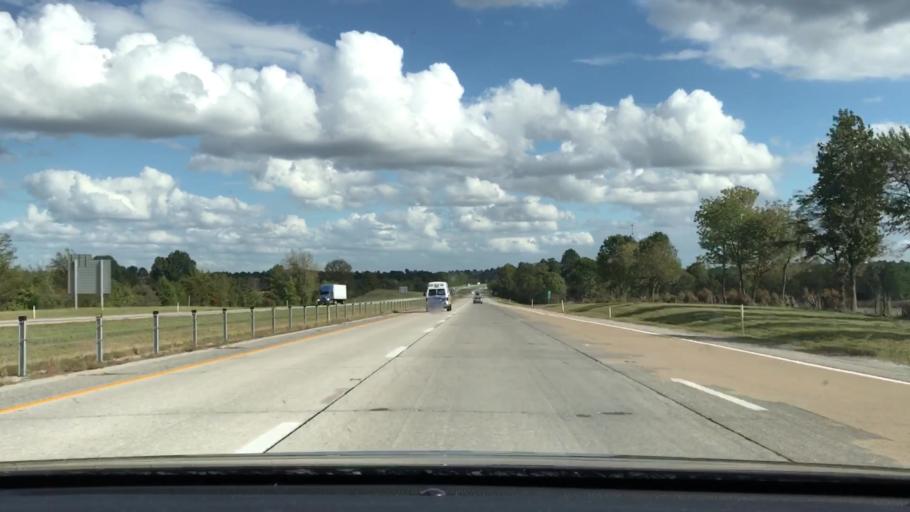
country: US
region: Kentucky
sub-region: Trigg County
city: Cadiz
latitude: 36.9647
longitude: -87.8697
